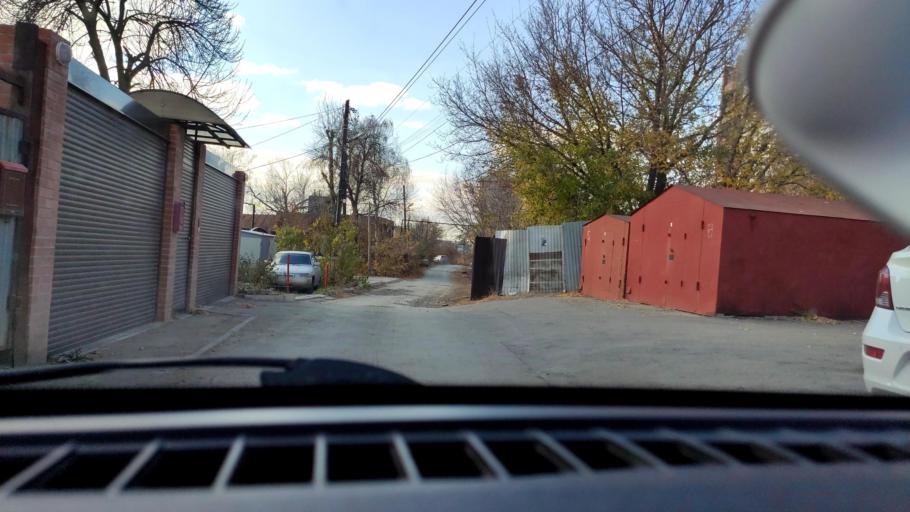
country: RU
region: Samara
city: Samara
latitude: 53.2215
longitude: 50.1783
